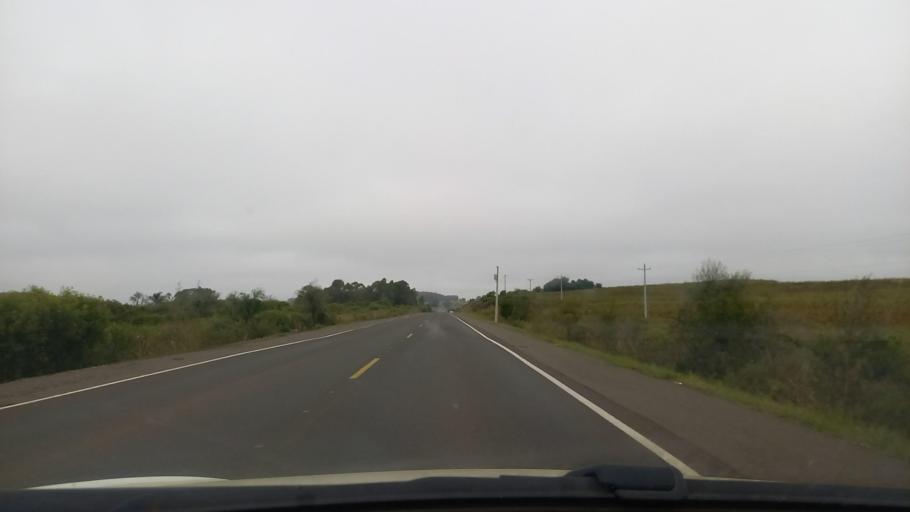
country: BR
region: Rio Grande do Sul
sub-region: Rosario Do Sul
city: Rosario do Sul
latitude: -30.3081
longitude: -54.9948
